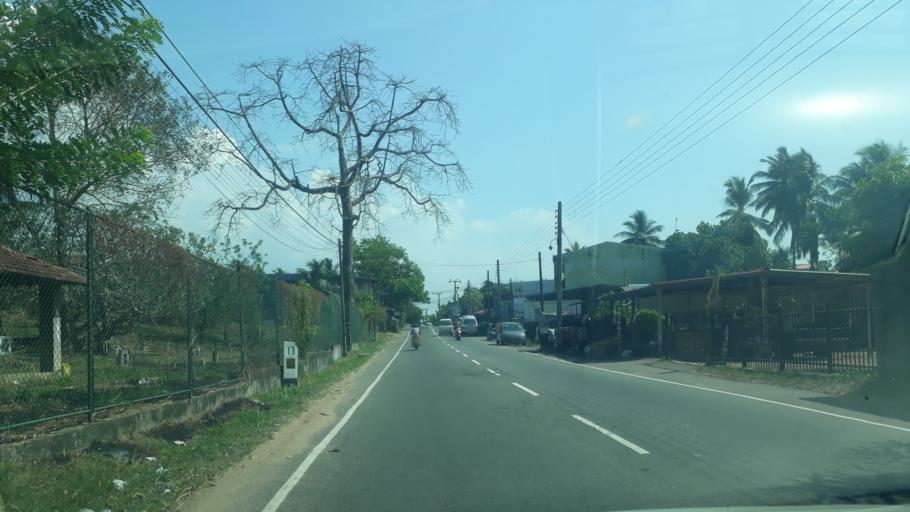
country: LK
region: Western
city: Gampaha
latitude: 7.0806
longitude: 80.0119
